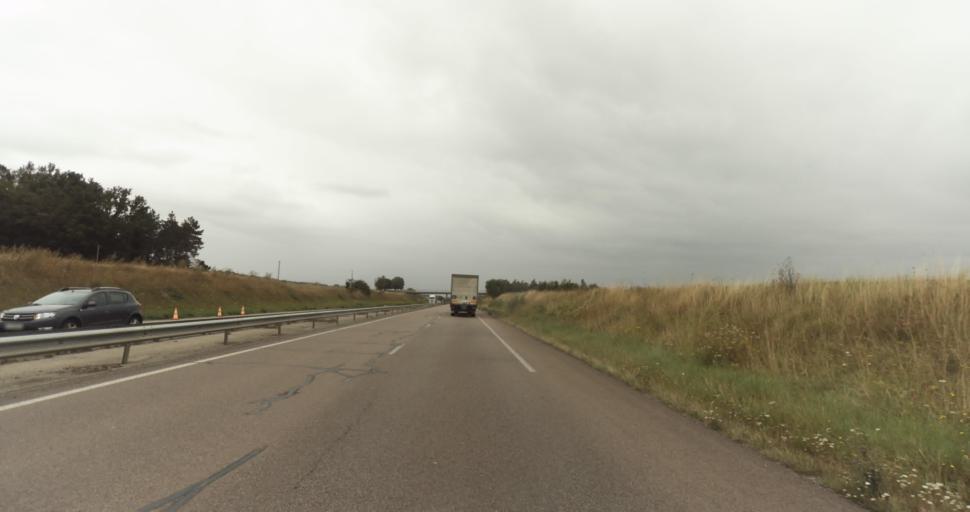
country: FR
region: Haute-Normandie
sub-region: Departement de l'Eure
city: Heudreville-sur-Eure
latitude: 49.1301
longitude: 1.1834
